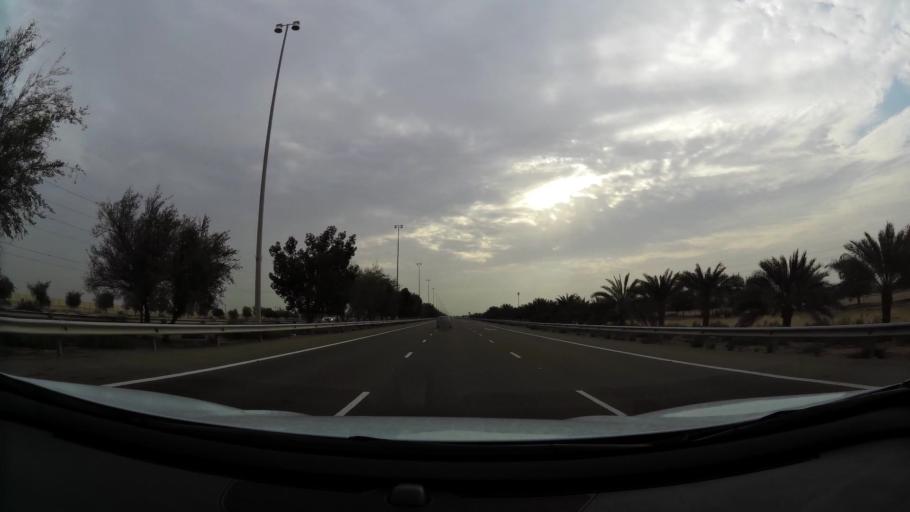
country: AE
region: Abu Dhabi
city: Abu Dhabi
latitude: 24.2194
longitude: 54.8446
